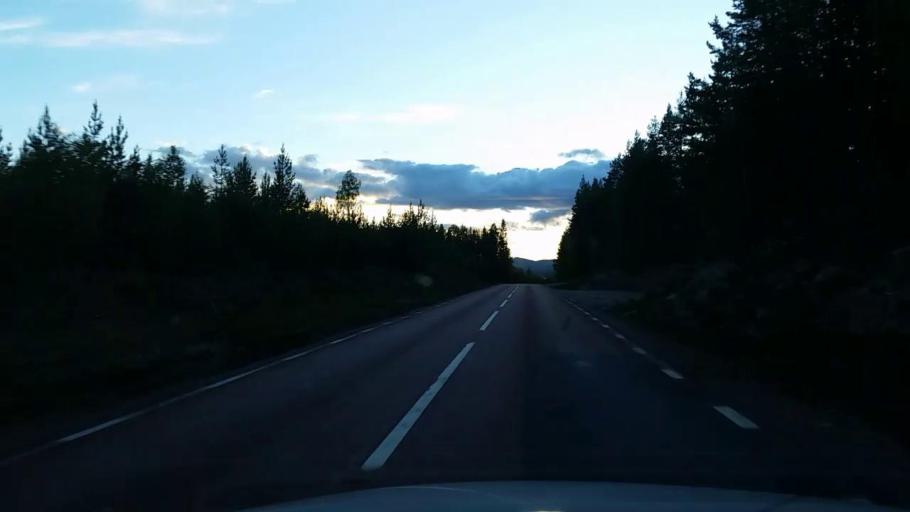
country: SE
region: Gaevleborg
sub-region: Ljusdals Kommun
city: Farila
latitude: 62.1006
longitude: 15.7842
